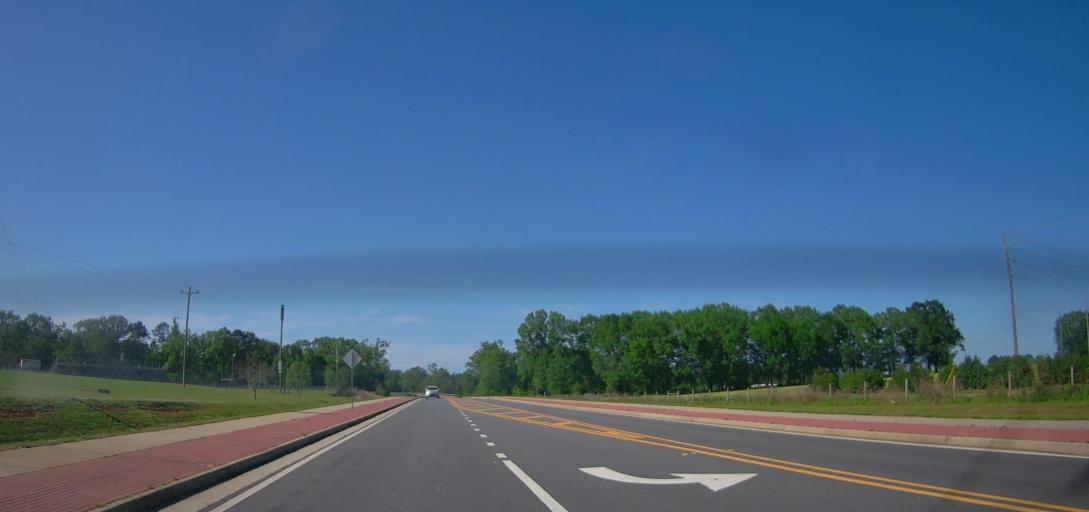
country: US
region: Georgia
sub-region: Houston County
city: Robins Air Force Base
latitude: 32.5443
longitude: -83.5846
